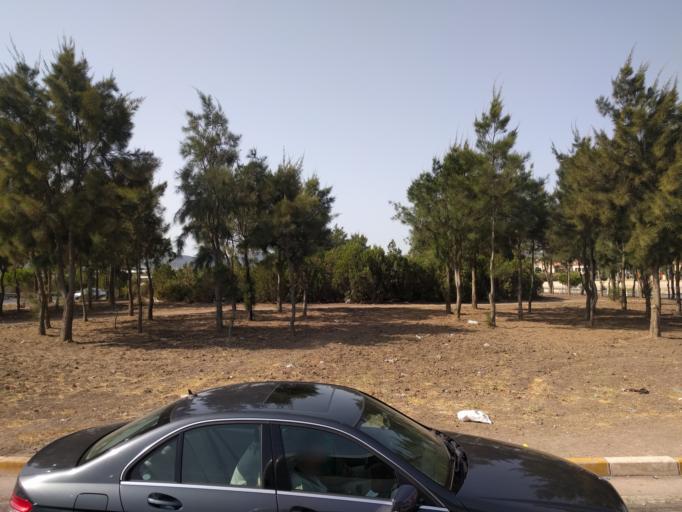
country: TR
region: Izmir
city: Alacati
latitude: 38.2888
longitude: 26.3855
